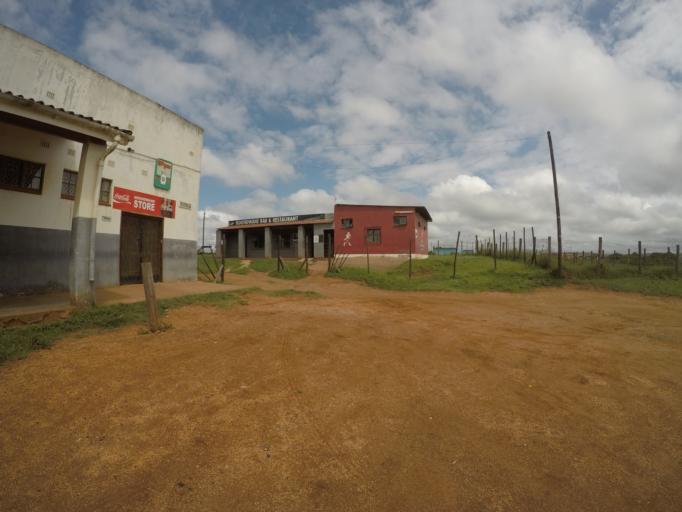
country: ZA
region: KwaZulu-Natal
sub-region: uThungulu District Municipality
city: Empangeni
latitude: -28.6040
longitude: 31.8460
